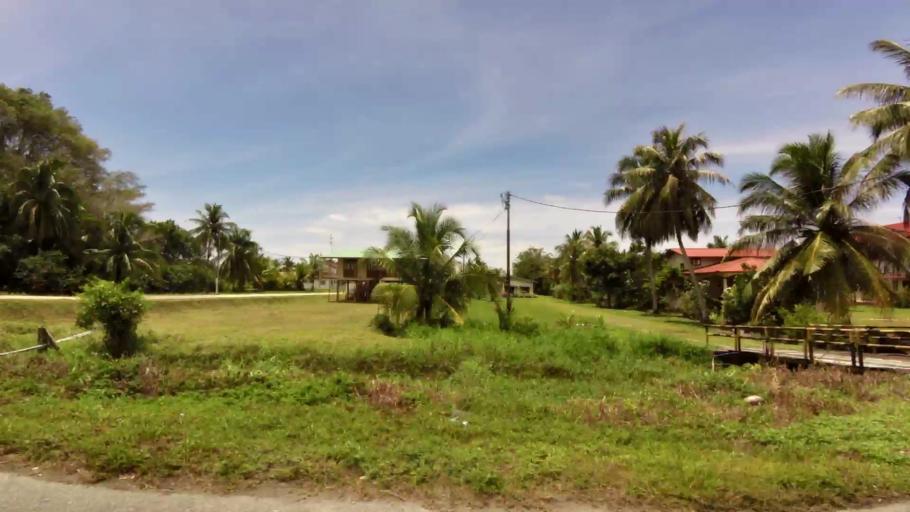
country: BN
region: Belait
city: Kuala Belait
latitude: 4.5850
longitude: 114.2492
